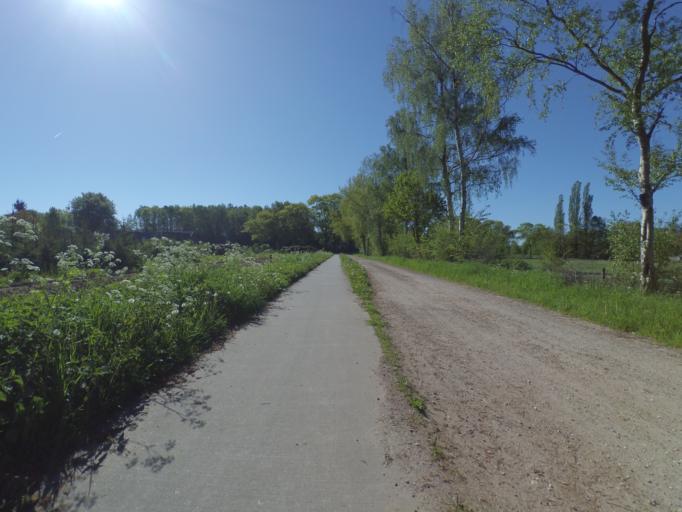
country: NL
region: Gelderland
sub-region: Gemeente Brummen
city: Brummen
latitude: 52.0976
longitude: 6.1217
